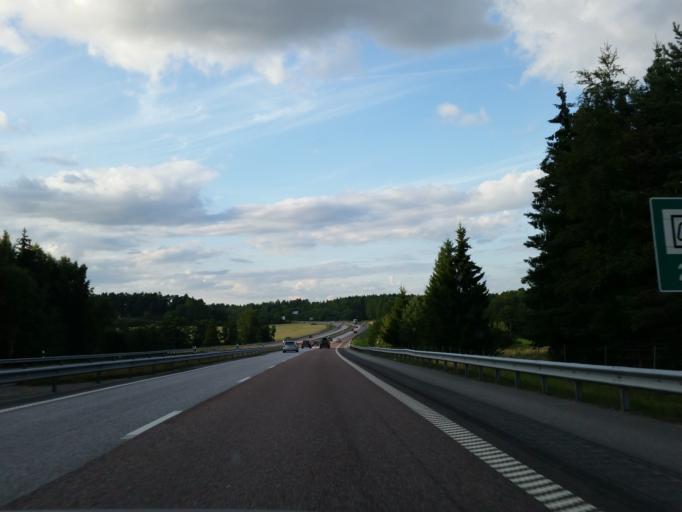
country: SE
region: Stockholm
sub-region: Sodertalje Kommun
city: Pershagen
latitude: 59.1380
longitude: 17.6472
